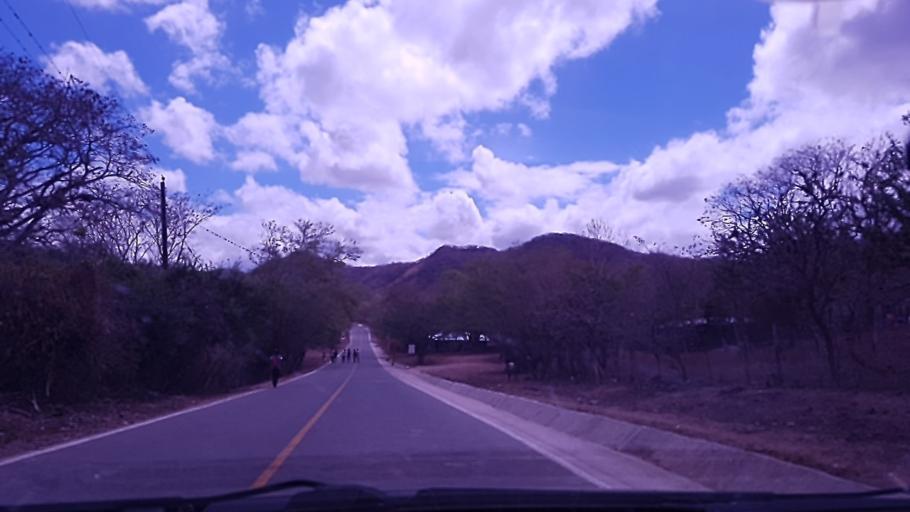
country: NI
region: Esteli
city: Condega
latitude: 13.3773
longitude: -86.3662
